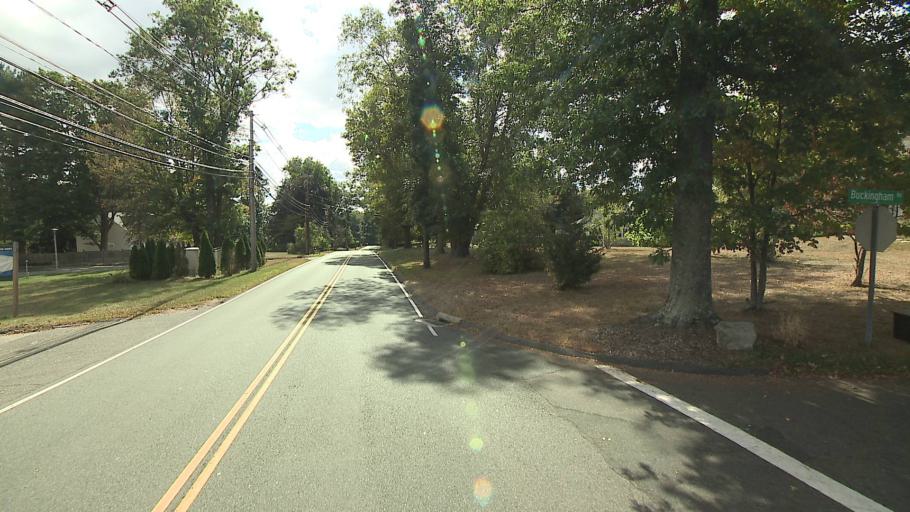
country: US
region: Connecticut
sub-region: New Haven County
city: Ansonia
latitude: 41.3566
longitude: -73.1113
